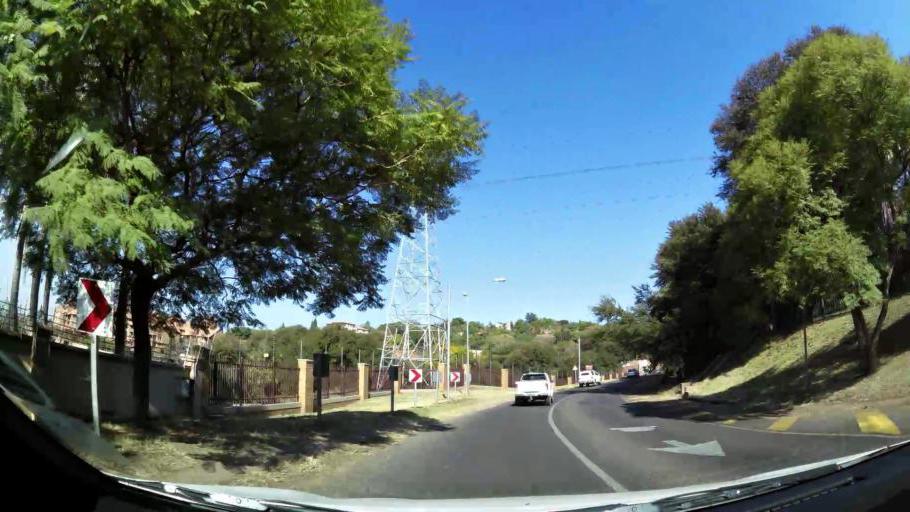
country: ZA
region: Gauteng
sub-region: City of Tshwane Metropolitan Municipality
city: Pretoria
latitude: -25.7989
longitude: 28.2716
